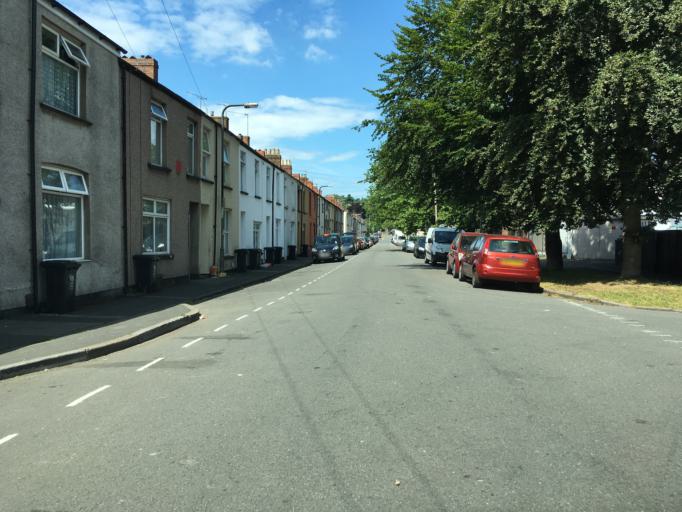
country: GB
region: Wales
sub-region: Newport
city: Newport
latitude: 51.5774
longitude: -2.9944
